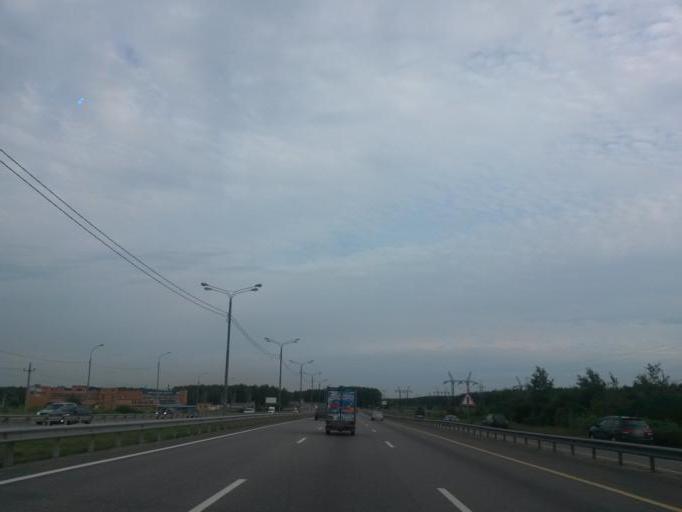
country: RU
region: Moskovskaya
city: Vostryakovo
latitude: 55.3724
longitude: 37.7810
